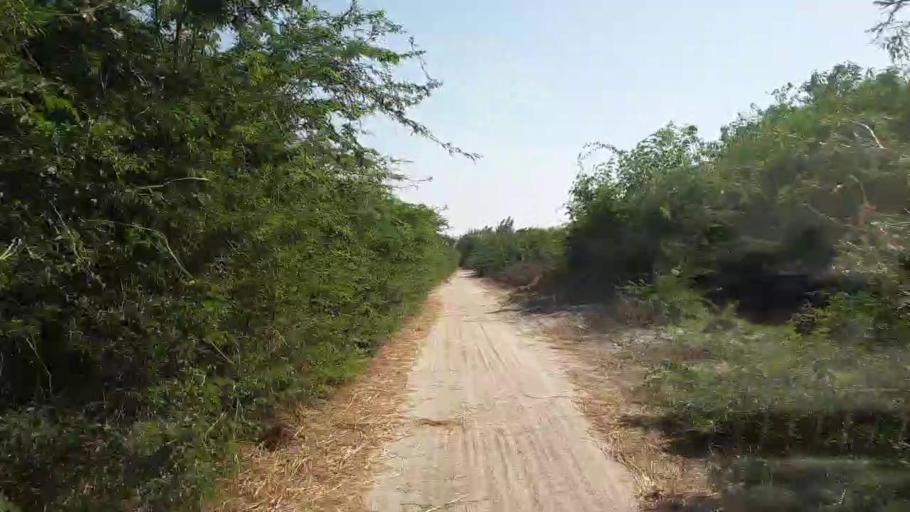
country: PK
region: Sindh
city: Tando Bago
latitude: 24.6502
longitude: 68.9839
